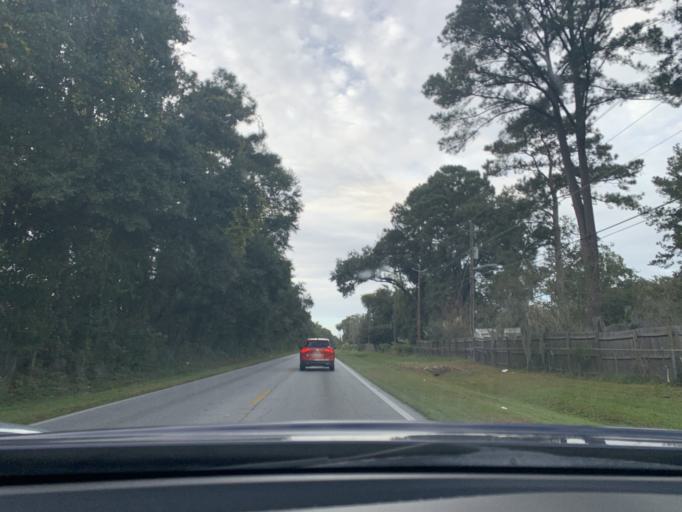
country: US
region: Georgia
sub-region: Chatham County
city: Georgetown
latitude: 32.0226
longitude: -81.2423
